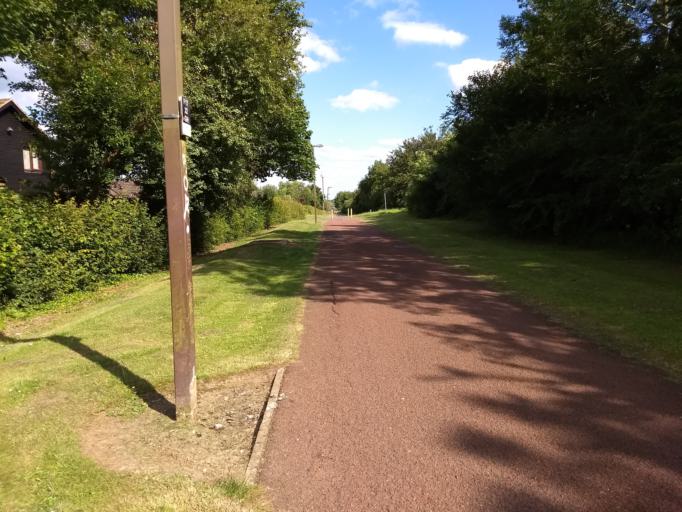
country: GB
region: England
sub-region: Milton Keynes
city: Shenley Church End
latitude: 52.0334
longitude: -0.8013
